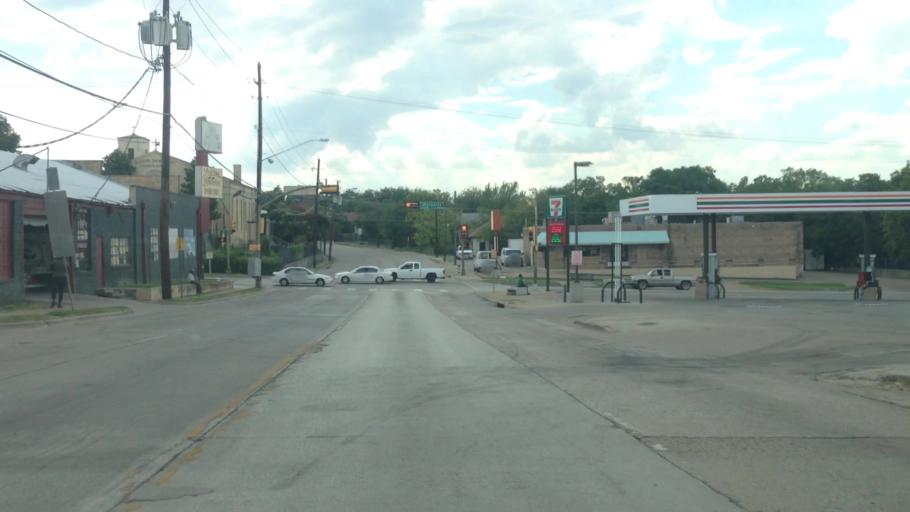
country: US
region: Texas
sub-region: Dallas County
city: Dallas
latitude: 32.7512
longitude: -96.8148
